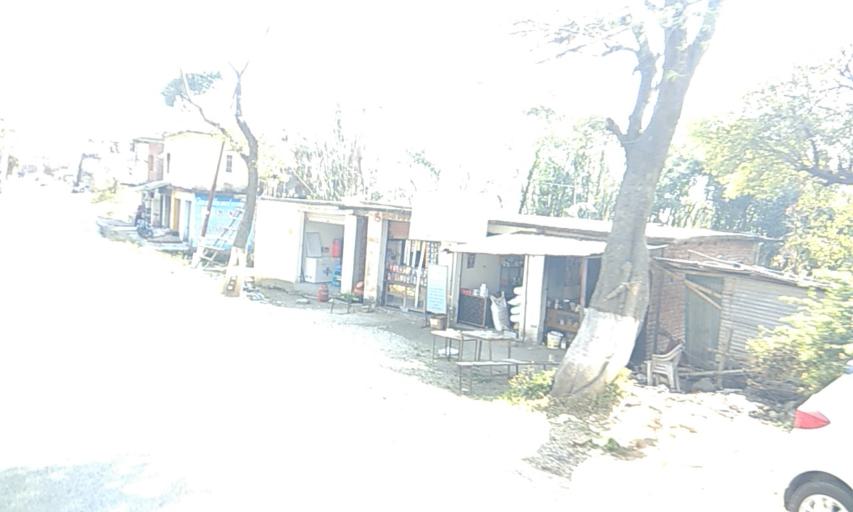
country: IN
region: Himachal Pradesh
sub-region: Kangra
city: Dharmsala
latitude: 32.1701
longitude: 76.3905
